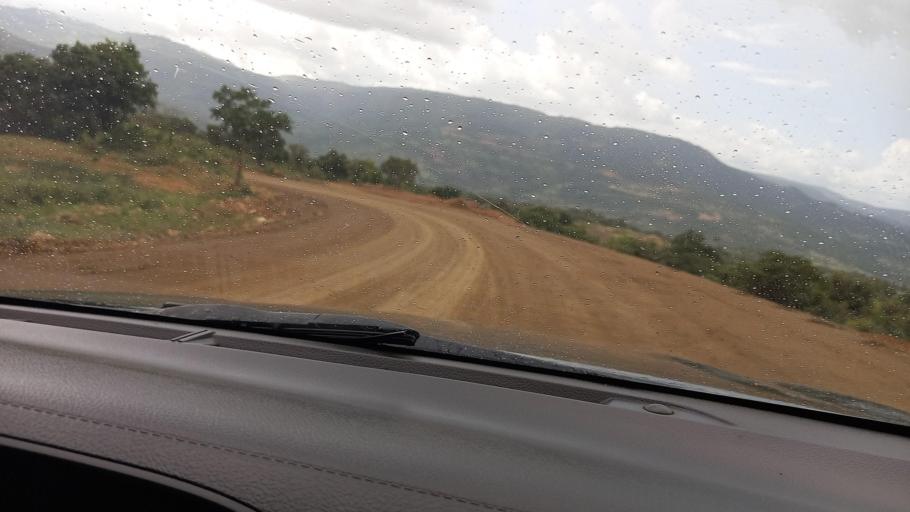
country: ET
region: Southern Nations, Nationalities, and People's Region
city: Mizan Teferi
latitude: 6.1822
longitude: 35.6952
